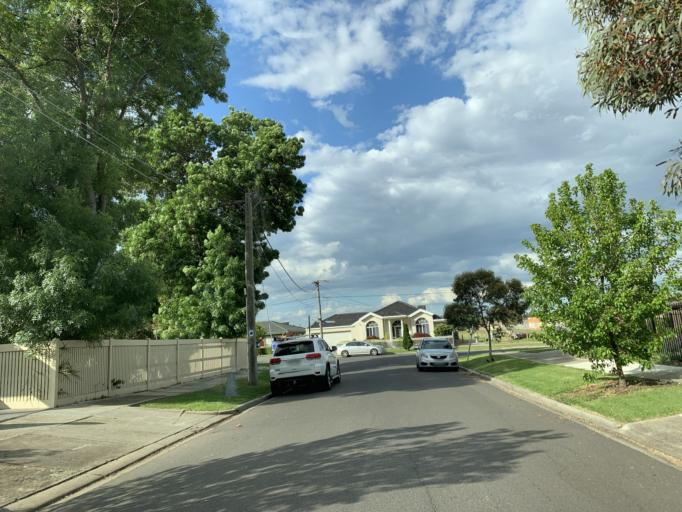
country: AU
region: Victoria
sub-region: Moonee Valley
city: Essendon West
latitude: -37.7543
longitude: 144.8557
